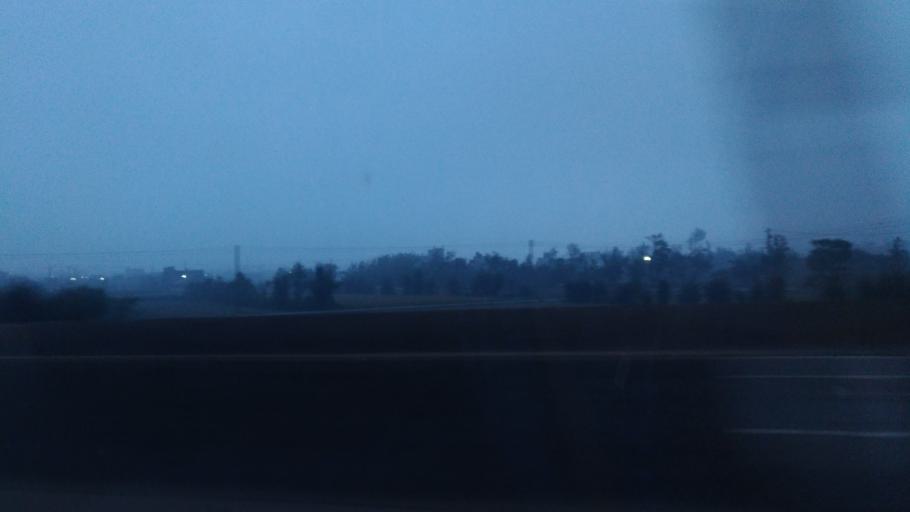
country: TW
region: Taiwan
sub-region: Miaoli
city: Miaoli
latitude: 24.6442
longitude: 120.7938
